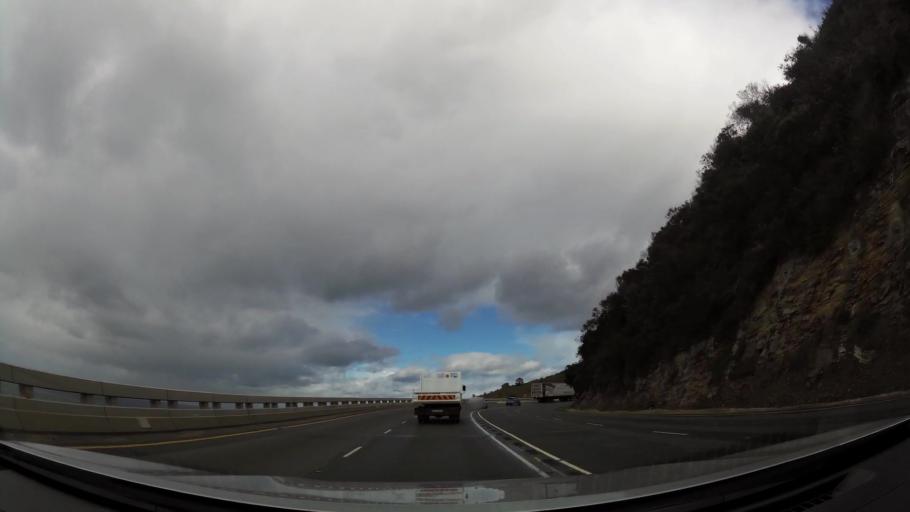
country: ZA
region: Western Cape
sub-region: Eden District Municipality
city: George
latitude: -33.9972
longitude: 22.5611
